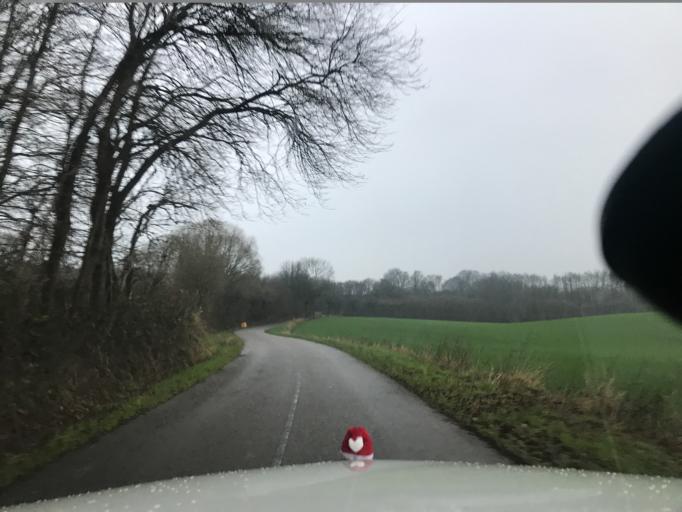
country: DK
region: South Denmark
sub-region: Sonderborg Kommune
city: Grasten
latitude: 54.8833
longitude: 9.5641
